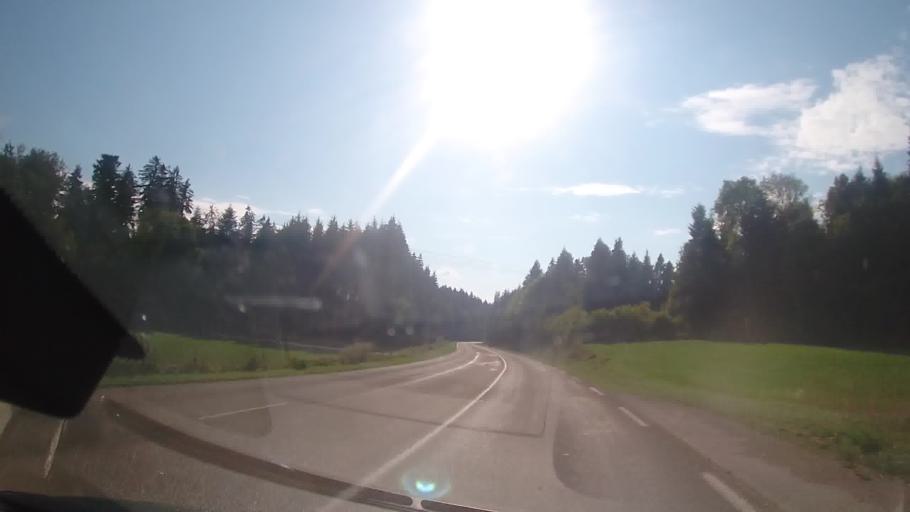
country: FR
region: Franche-Comte
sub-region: Departement du Jura
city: Clairvaux-les-Lacs
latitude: 46.5821
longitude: 5.7885
